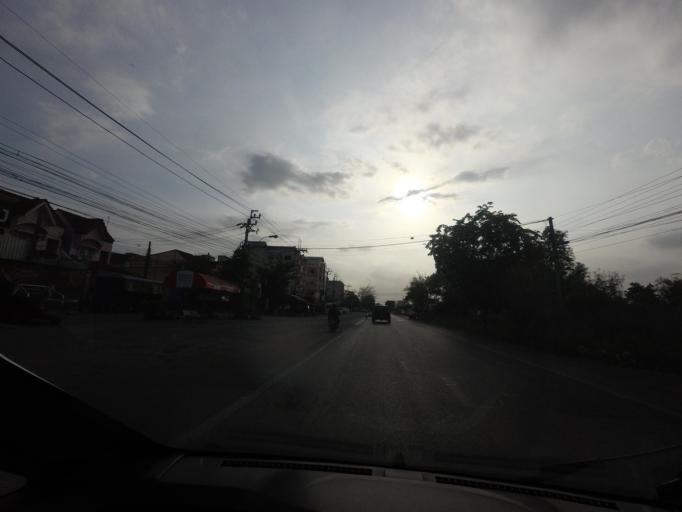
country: TH
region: Bangkok
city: Nong Chok
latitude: 13.8501
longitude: 100.8842
